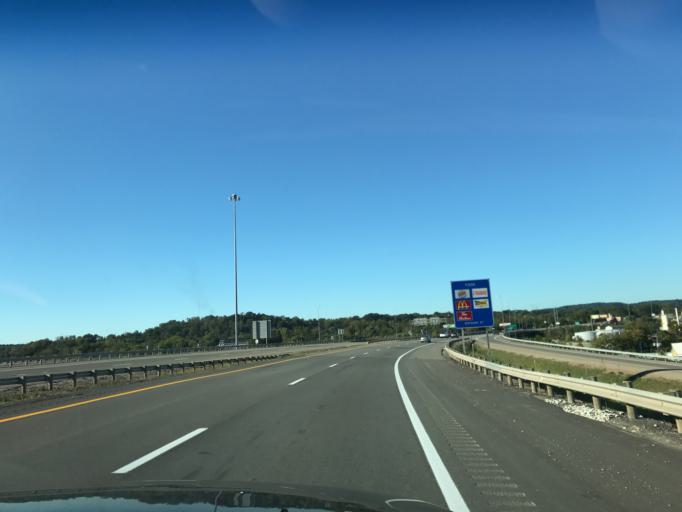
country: US
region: West Virginia
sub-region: Wood County
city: Parkersburg
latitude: 39.2579
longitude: -81.5314
